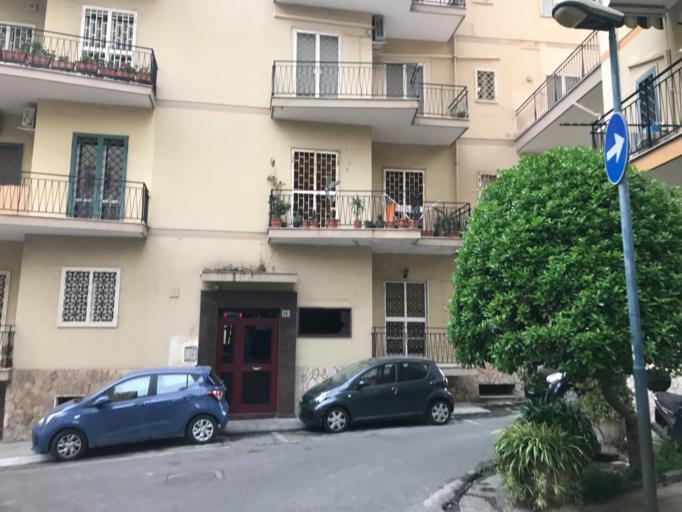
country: IT
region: Campania
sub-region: Provincia di Napoli
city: Napoli
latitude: 40.8540
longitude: 14.2221
